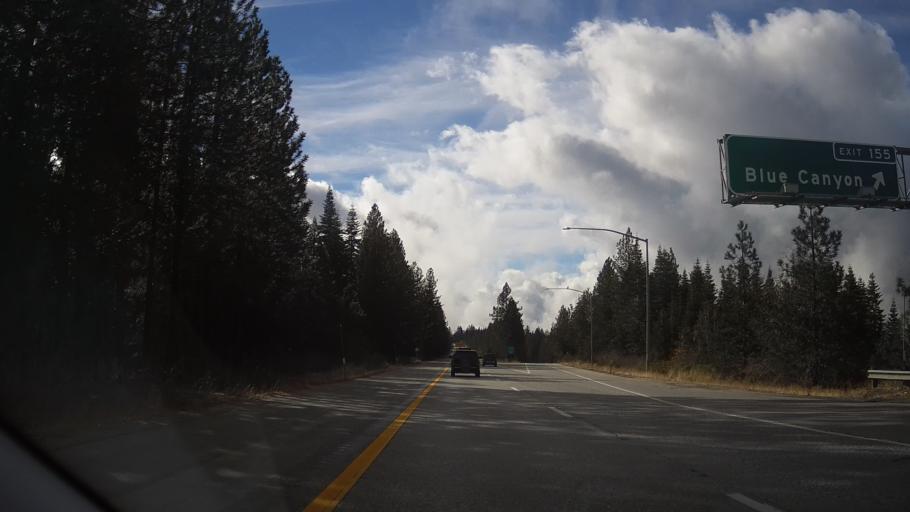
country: US
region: California
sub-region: Placer County
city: Foresthill
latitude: 39.2863
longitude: -120.6994
